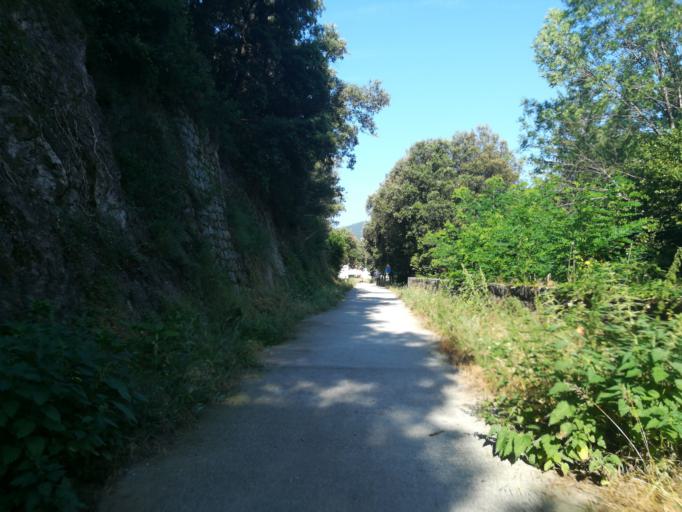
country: FR
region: Languedoc-Roussillon
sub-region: Departement des Pyrenees-Orientales
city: Reiners
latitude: 42.4831
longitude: 2.6899
